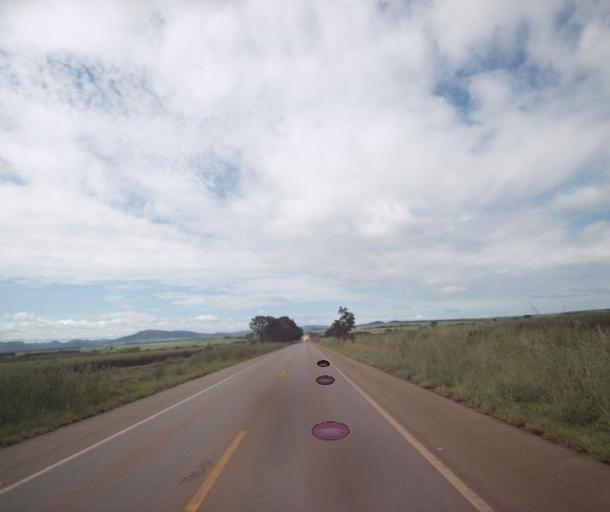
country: BR
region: Goias
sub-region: Barro Alto
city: Barro Alto
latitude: -15.0355
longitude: -48.8920
